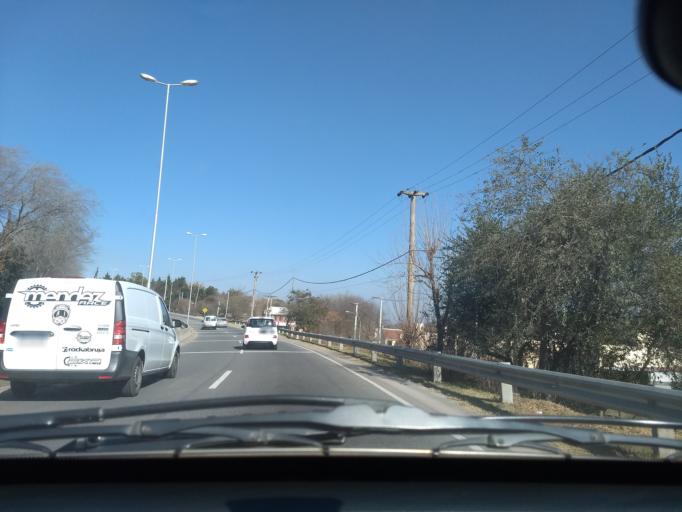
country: AR
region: Cordoba
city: Rio Ceballos
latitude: -31.1699
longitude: -64.3032
